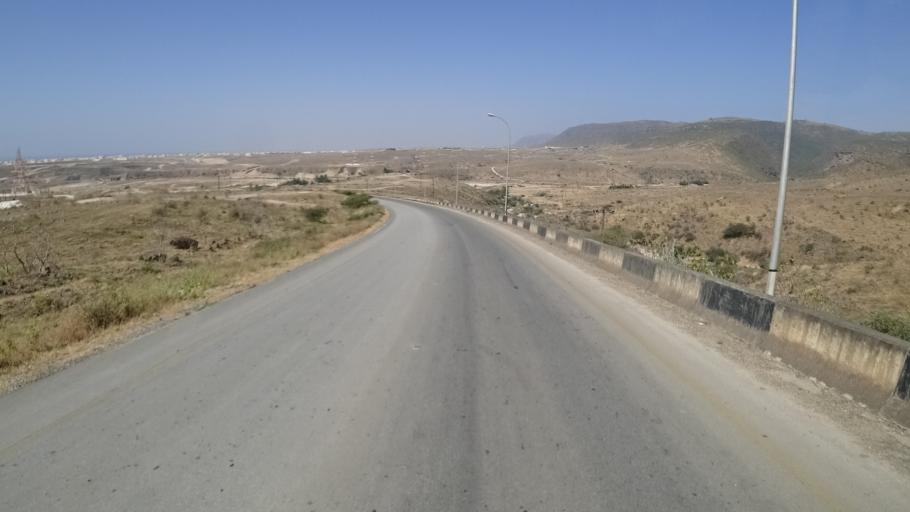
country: OM
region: Zufar
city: Salalah
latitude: 17.0662
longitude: 54.4410
